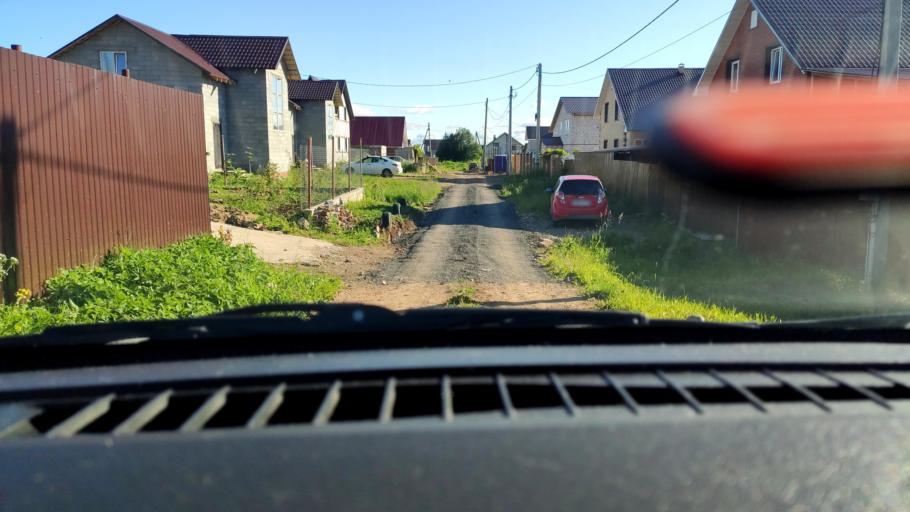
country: RU
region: Perm
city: Kultayevo
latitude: 57.8622
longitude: 55.9108
